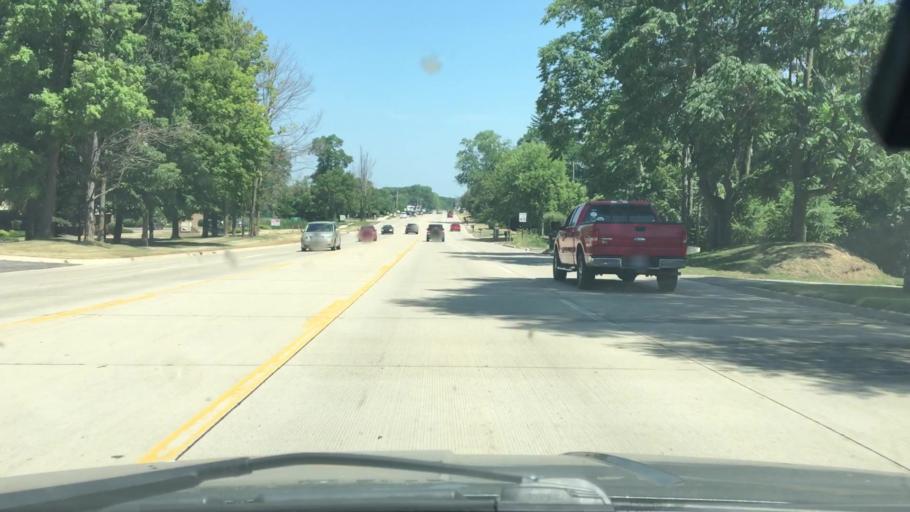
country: US
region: Michigan
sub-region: Livingston County
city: Brighton
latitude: 42.5194
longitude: -83.7518
